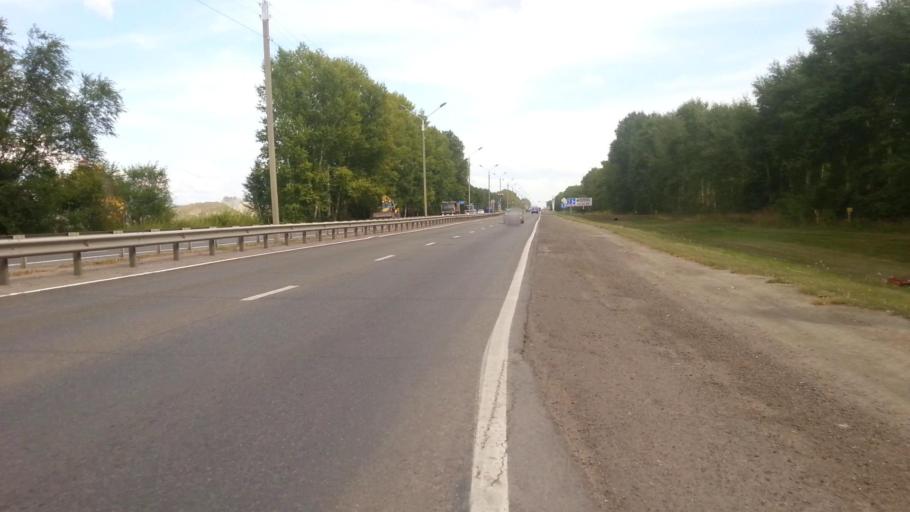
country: RU
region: Altai Krai
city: Vlasikha
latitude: 53.3532
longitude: 83.5592
